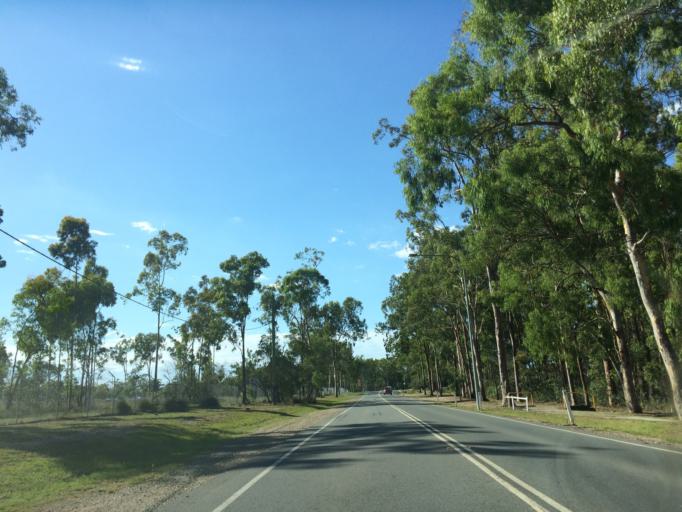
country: AU
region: Queensland
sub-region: Logan
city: Park Ridge South
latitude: -27.7074
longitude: 152.9764
